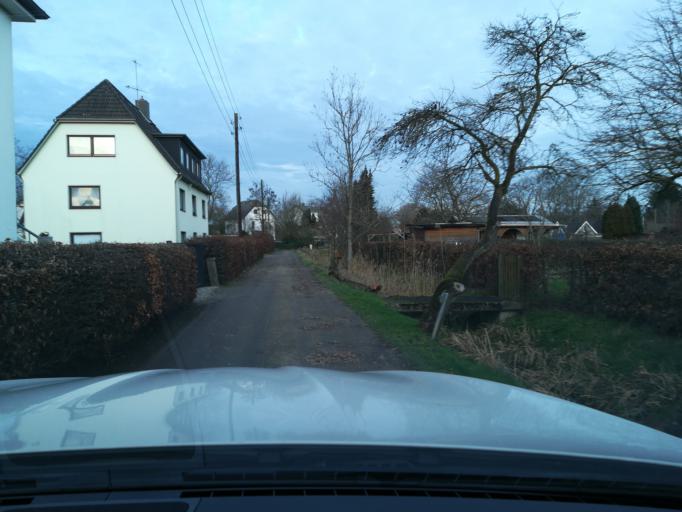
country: DE
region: Hamburg
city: Harburg
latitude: 53.4672
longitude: 10.0107
